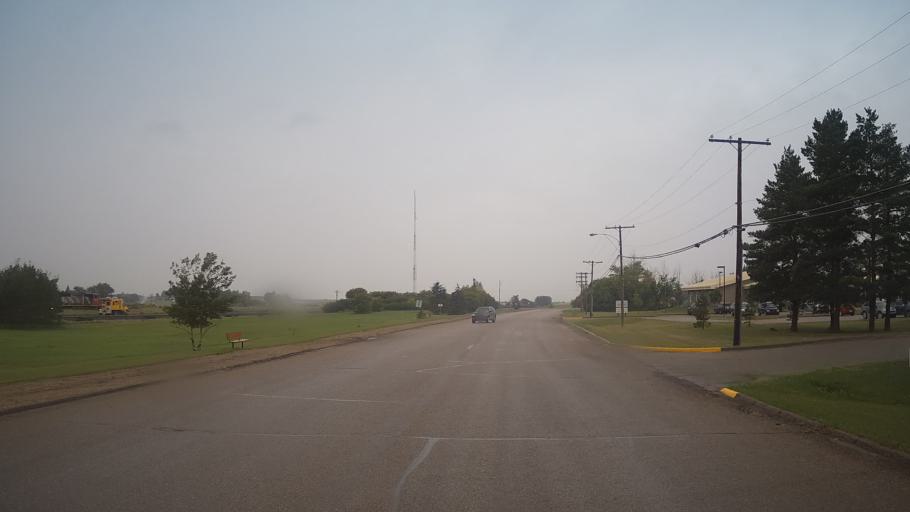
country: CA
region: Saskatchewan
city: Biggar
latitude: 52.0564
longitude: -107.9958
